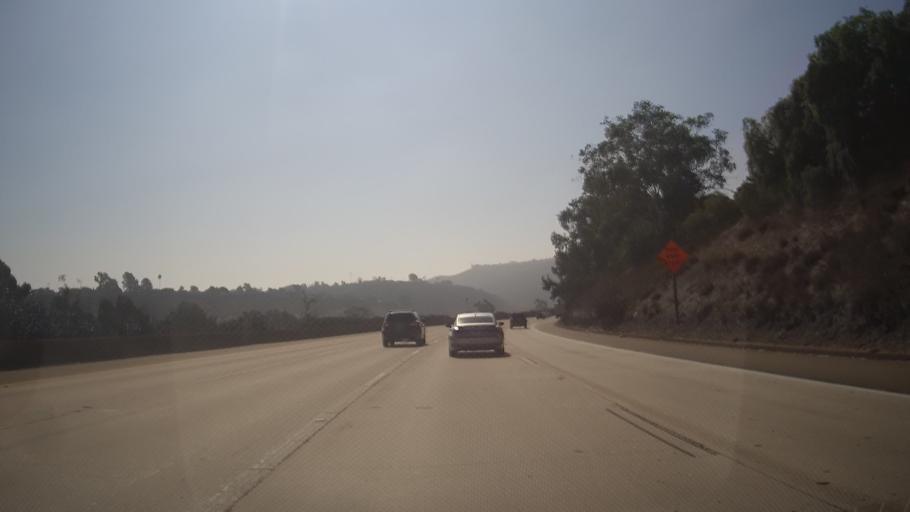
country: US
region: California
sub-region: San Diego County
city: La Jolla
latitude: 32.8570
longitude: -117.2317
